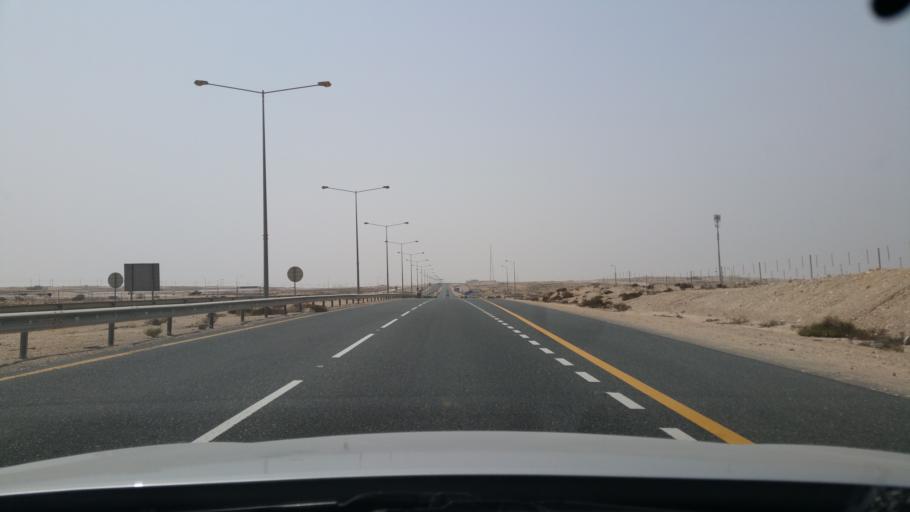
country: QA
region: Baladiyat ar Rayyan
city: Dukhan
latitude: 25.3270
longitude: 50.7865
